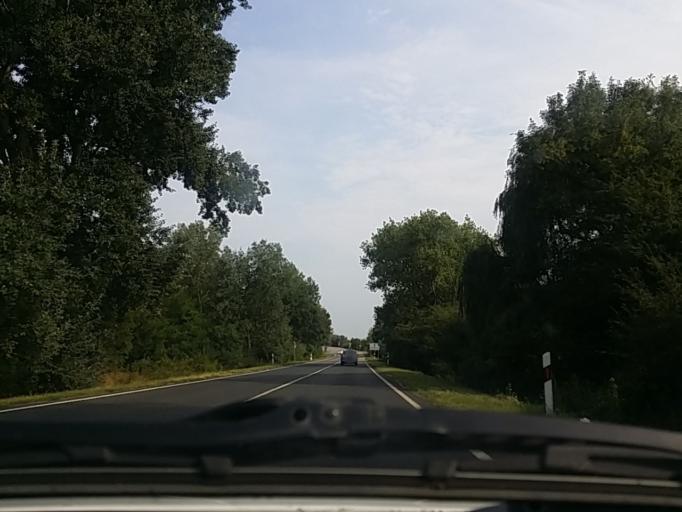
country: HU
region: Fejer
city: Szarliget
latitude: 47.4956
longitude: 18.5100
